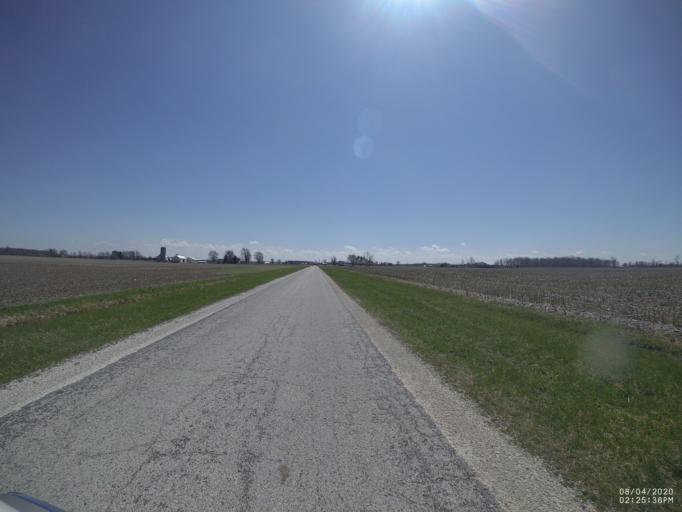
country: US
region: Ohio
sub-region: Sandusky County
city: Gibsonburg
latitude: 41.2958
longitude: -83.2596
